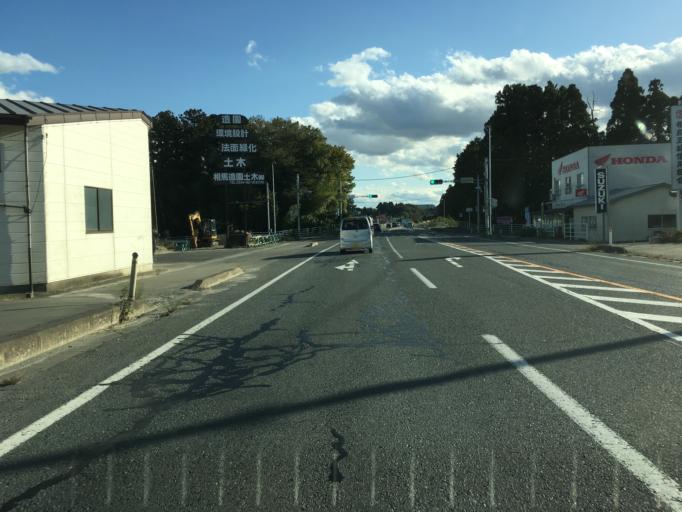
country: JP
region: Miyagi
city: Marumori
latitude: 37.8735
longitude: 140.9192
